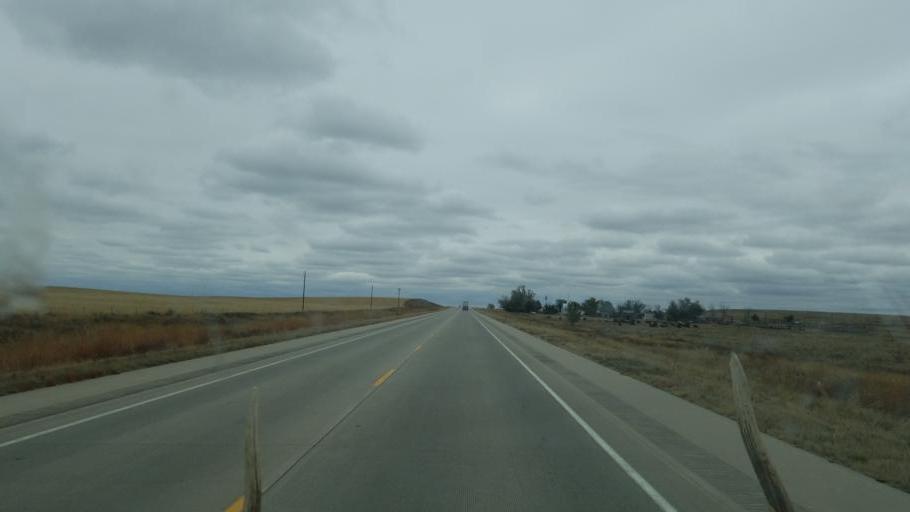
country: US
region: Colorado
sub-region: Kiowa County
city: Eads
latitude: 38.7255
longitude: -102.7761
